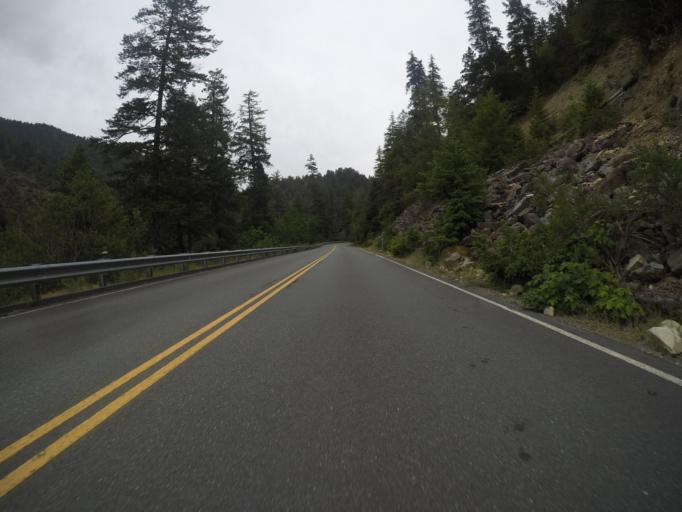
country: US
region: California
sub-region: Del Norte County
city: Bertsch-Oceanview
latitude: 41.7184
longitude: -123.9462
